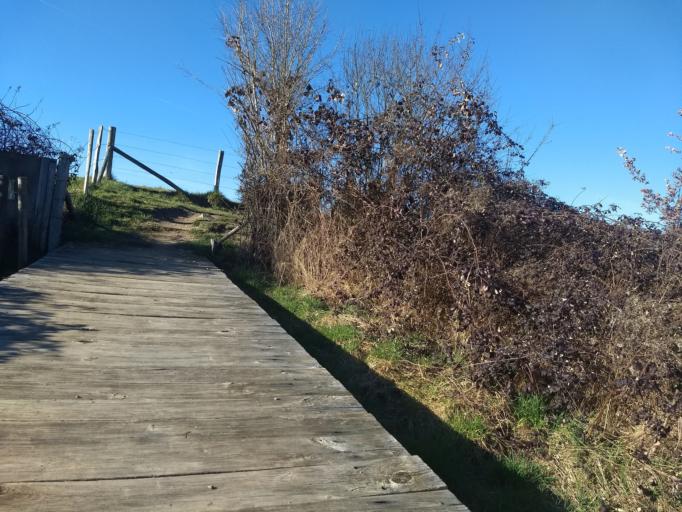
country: FR
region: Limousin
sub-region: Departement de la Haute-Vienne
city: Isle
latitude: 45.8282
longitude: 1.2124
